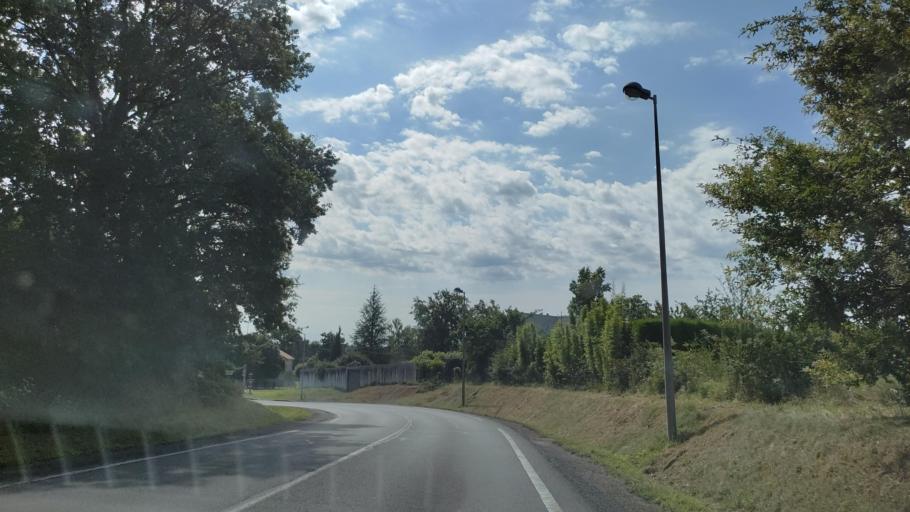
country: FR
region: Limousin
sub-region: Departement de la Haute-Vienne
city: Isle
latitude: 45.8355
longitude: 1.1930
